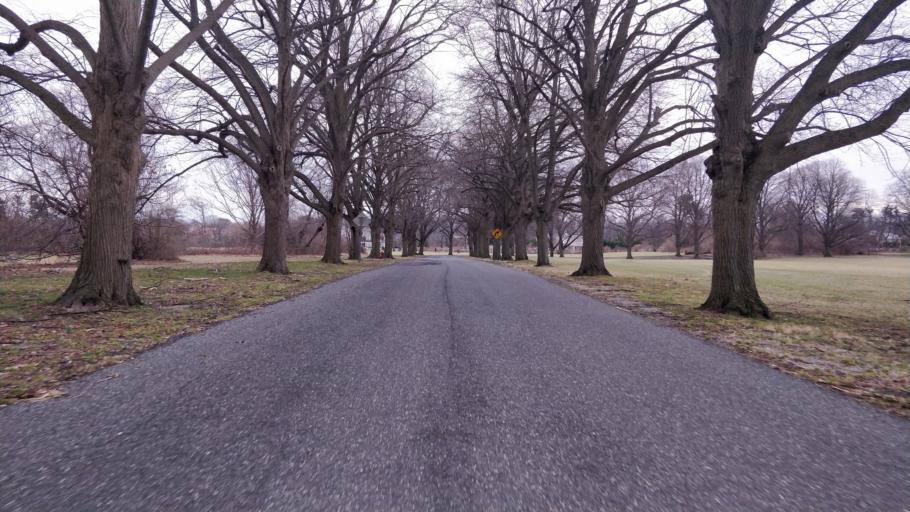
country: US
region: New York
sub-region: Nassau County
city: Old Westbury
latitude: 40.7868
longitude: -73.5763
